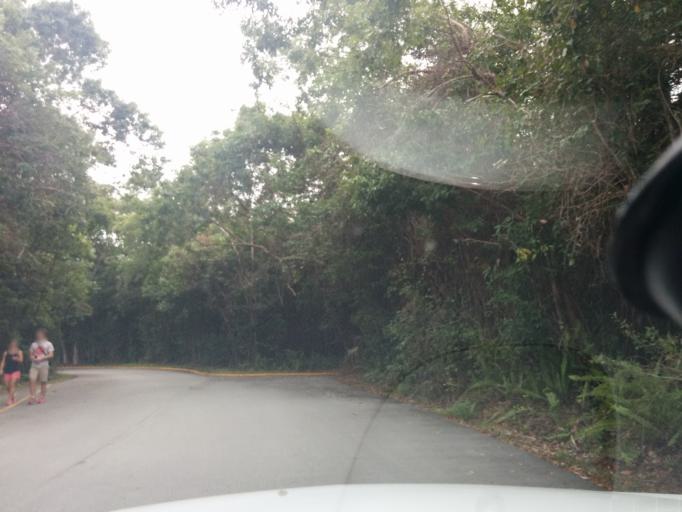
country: US
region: Florida
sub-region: Miami-Dade County
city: Florida City
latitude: 25.3828
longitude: -80.6103
